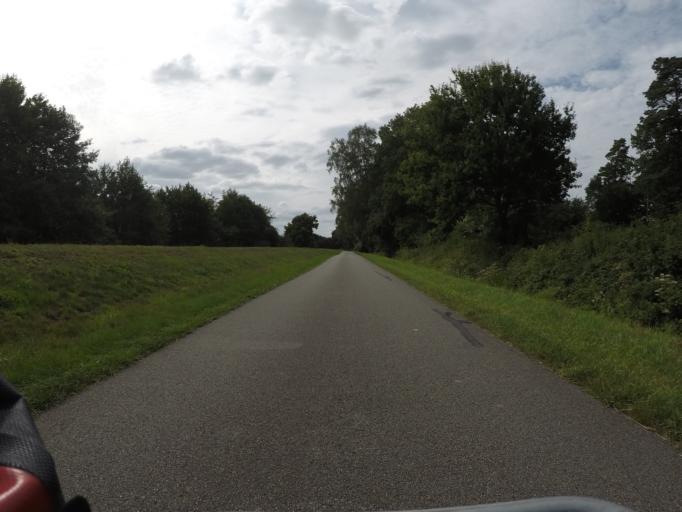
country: DE
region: Lower Saxony
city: Barum
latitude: 53.3413
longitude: 10.3947
